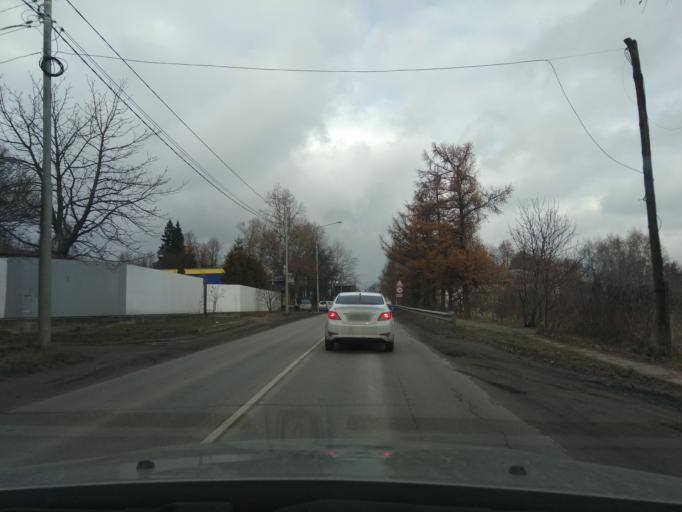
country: RU
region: Moscow
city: Zagor'ye
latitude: 55.5594
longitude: 37.6839
